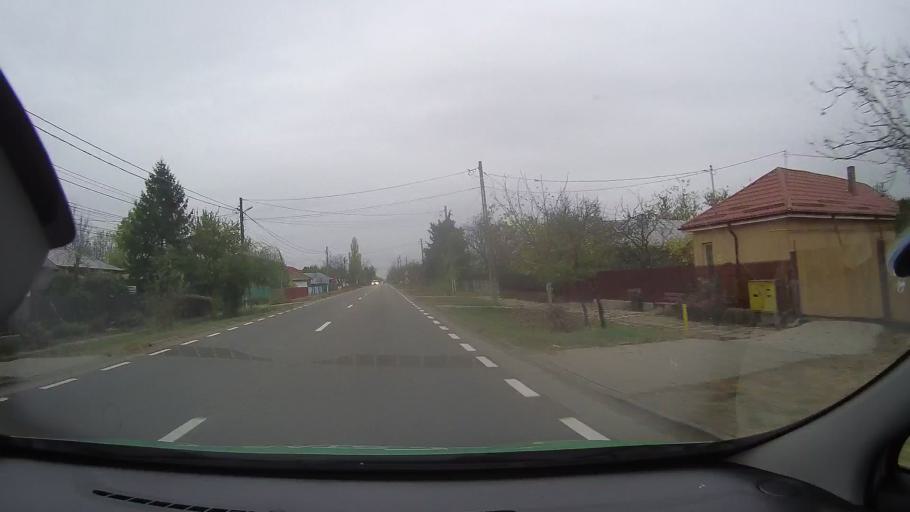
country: RO
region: Ialomita
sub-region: Comuna Slobozia
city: Slobozia
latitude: 44.6040
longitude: 27.3868
